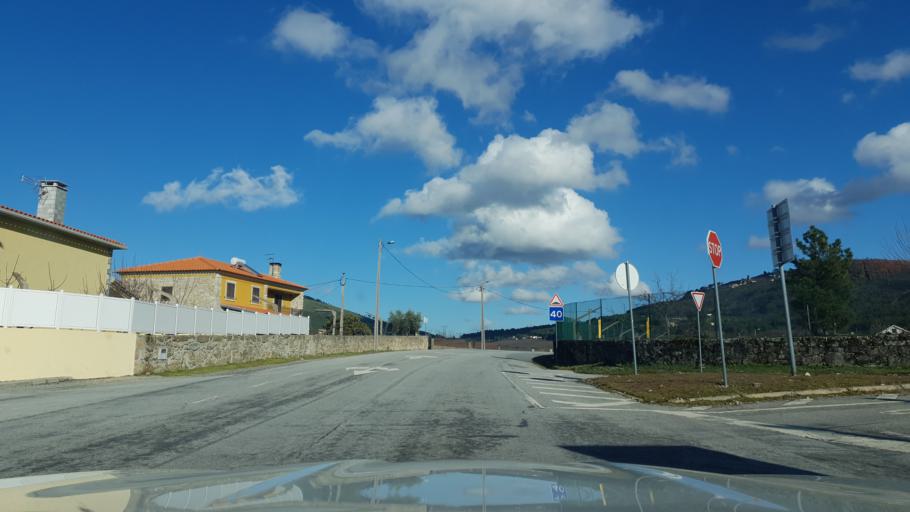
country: PT
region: Braganca
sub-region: Torre de Moncorvo
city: Torre de Moncorvo
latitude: 41.1831
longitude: -6.9811
